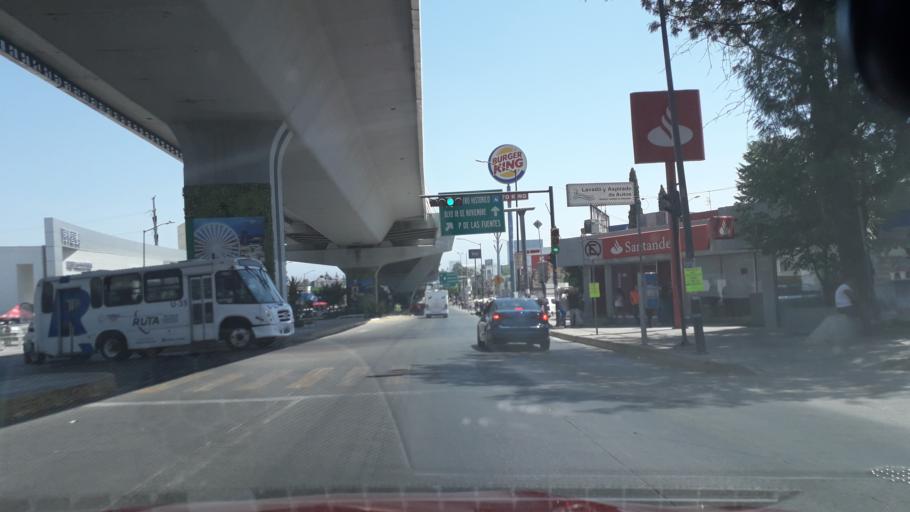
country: MX
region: Puebla
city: Puebla
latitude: 19.0630
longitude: -98.1811
